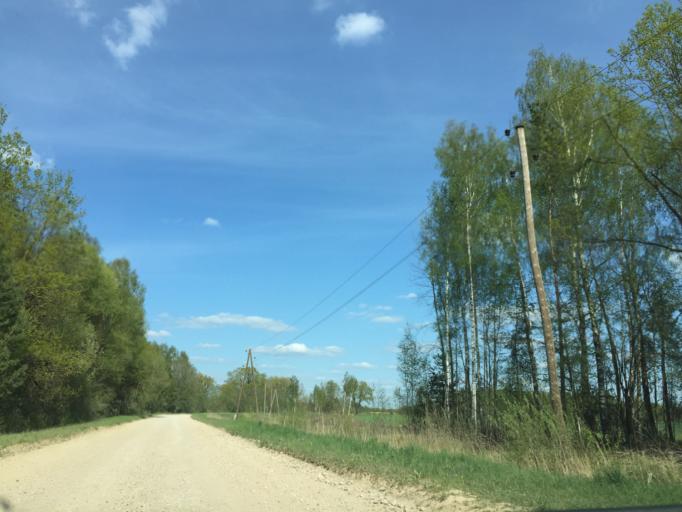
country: LV
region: Vecumnieki
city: Vecumnieki
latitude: 56.5102
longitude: 24.4068
